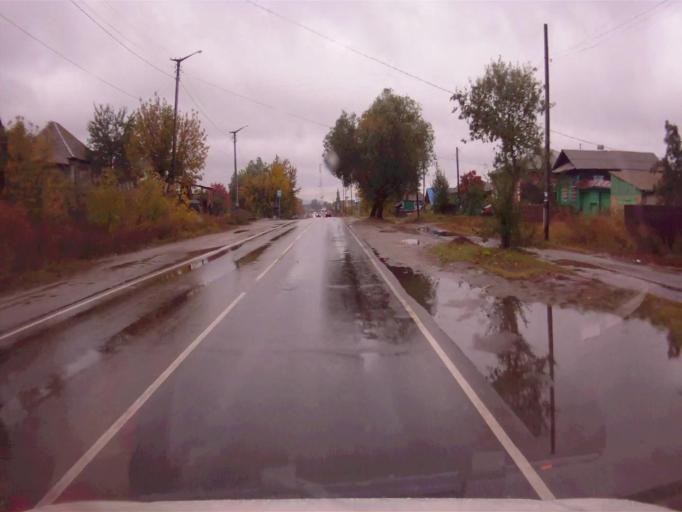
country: RU
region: Chelyabinsk
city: Kyshtym
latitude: 55.7125
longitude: 60.5581
